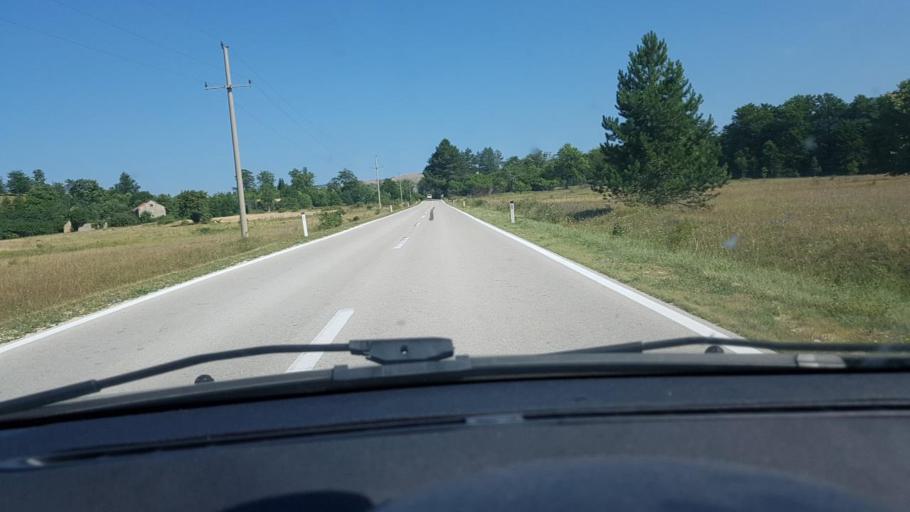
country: BA
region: Federation of Bosnia and Herzegovina
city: Bosansko Grahovo
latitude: 44.1049
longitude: 16.5499
